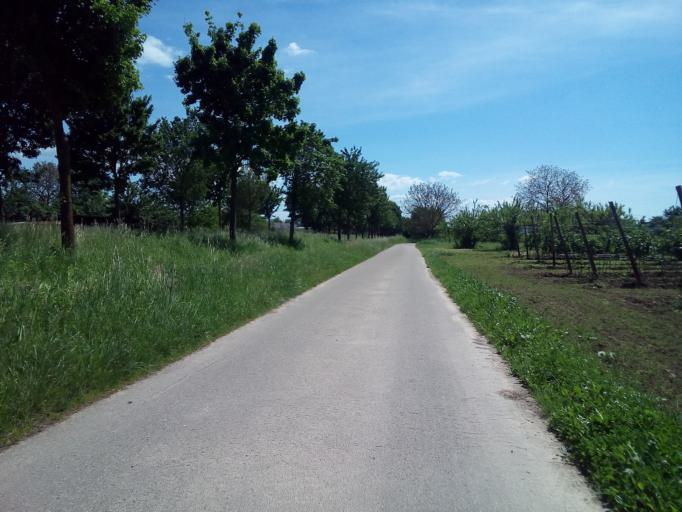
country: DE
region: Baden-Wuerttemberg
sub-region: Freiburg Region
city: Renchen
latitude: 48.5980
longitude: 8.0102
